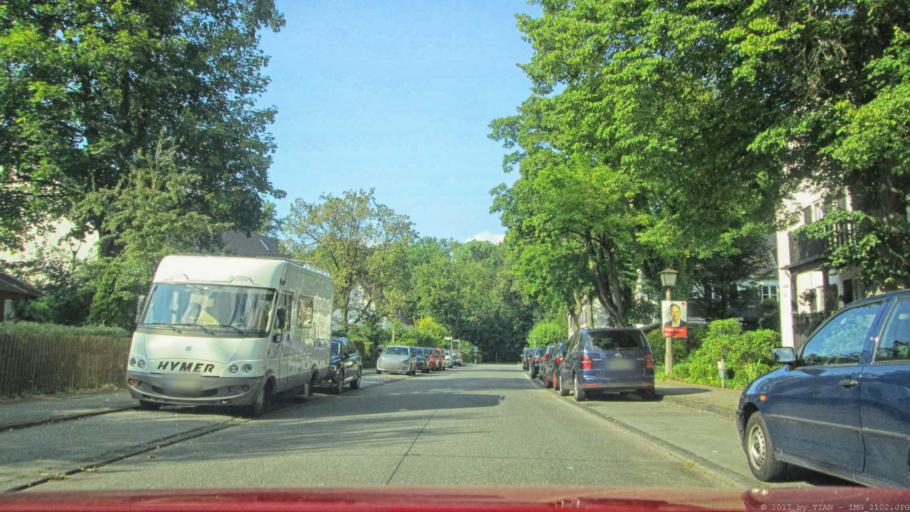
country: DE
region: Lower Saxony
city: Wolfsburg
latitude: 52.4150
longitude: 10.8090
